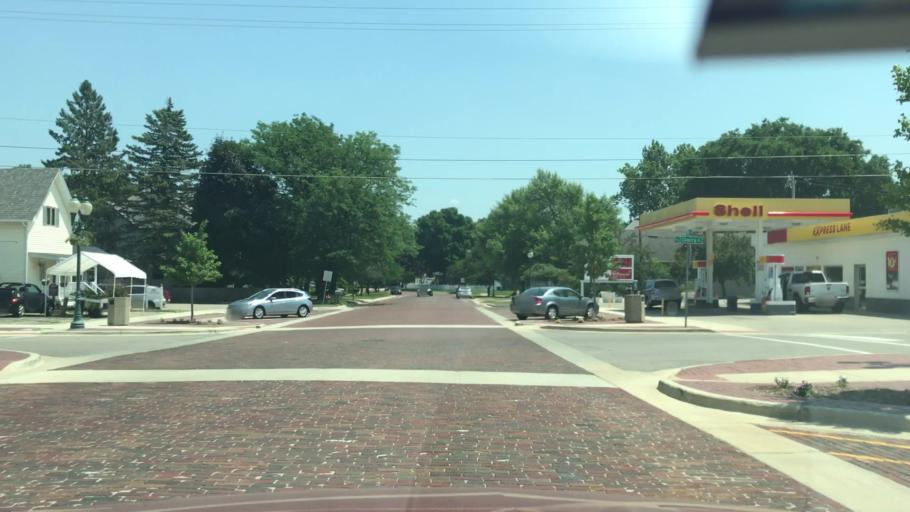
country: US
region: Illinois
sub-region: Winnebago County
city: Cherry Valley
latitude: 42.2352
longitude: -88.9522
